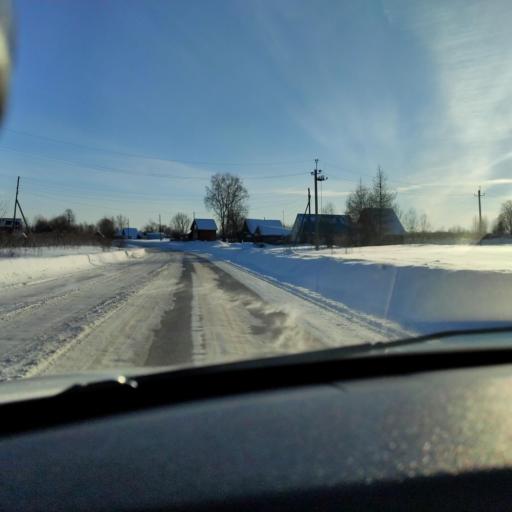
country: RU
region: Perm
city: Polazna
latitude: 58.3324
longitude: 56.4319
